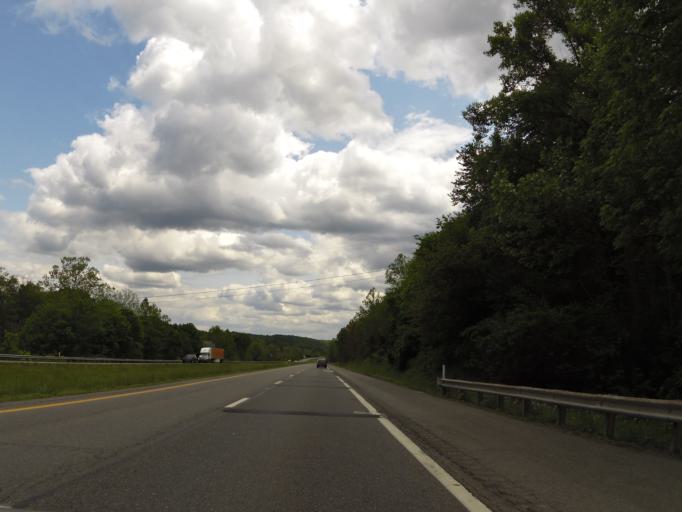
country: US
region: West Virginia
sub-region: Jackson County
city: Ripley
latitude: 38.7409
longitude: -81.6741
